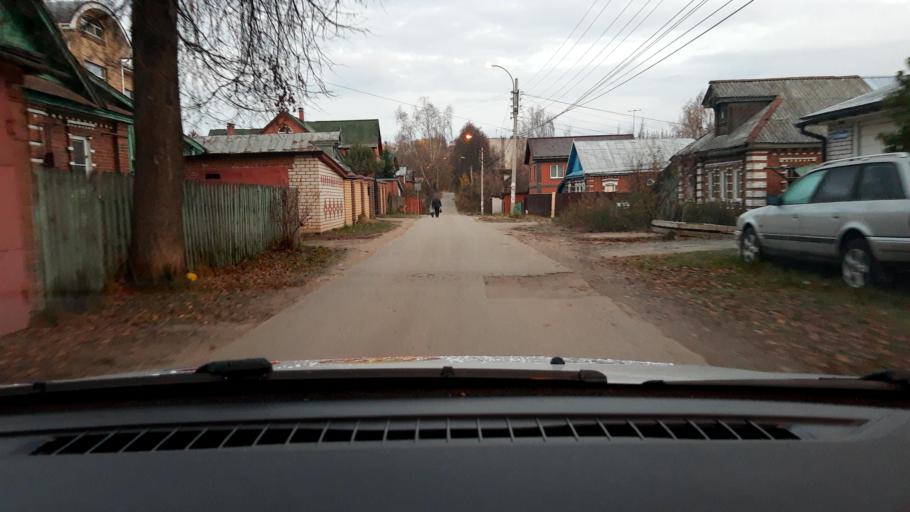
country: RU
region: Nizjnij Novgorod
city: Afonino
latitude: 56.2699
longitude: 44.0928
